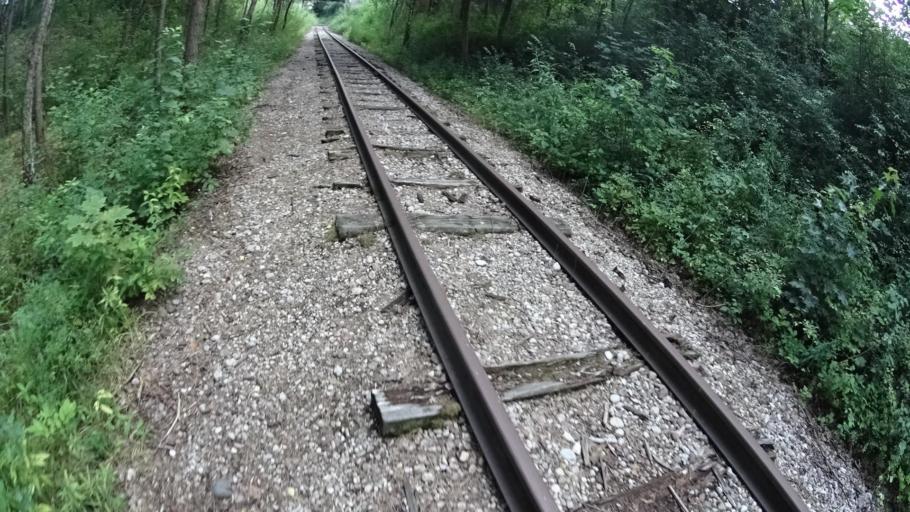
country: PL
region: Masovian Voivodeship
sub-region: Powiat piaseczynski
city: Tarczyn
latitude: 51.9701
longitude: 20.8693
